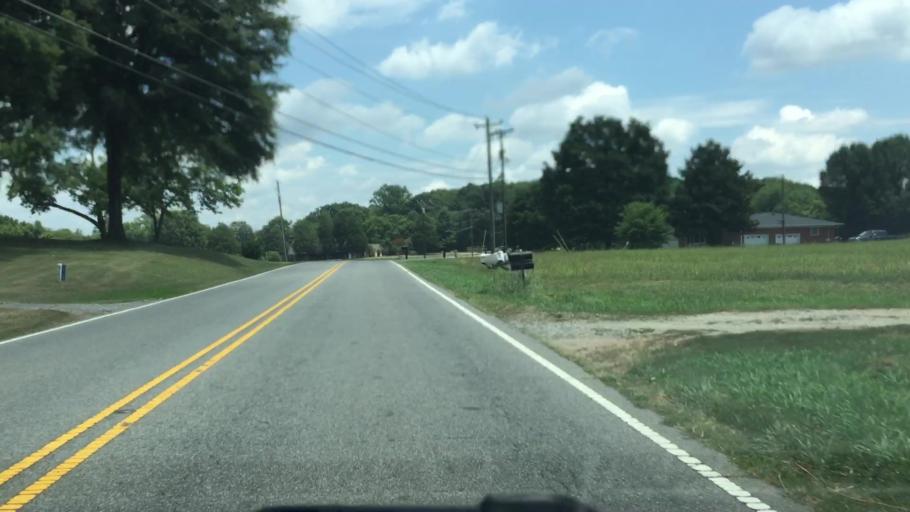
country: US
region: North Carolina
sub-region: Rowan County
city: Enochville
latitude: 35.4298
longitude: -80.7198
